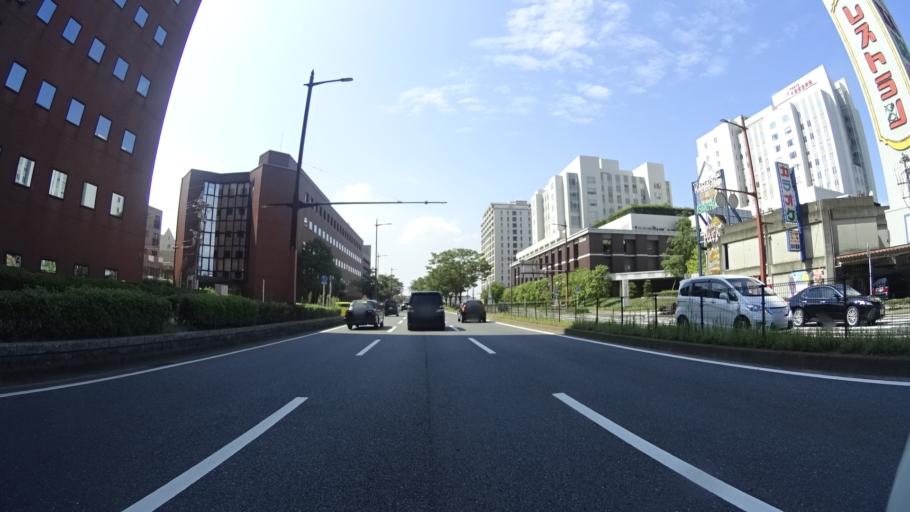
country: JP
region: Fukuoka
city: Kitakyushu
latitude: 33.8893
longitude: 130.8839
